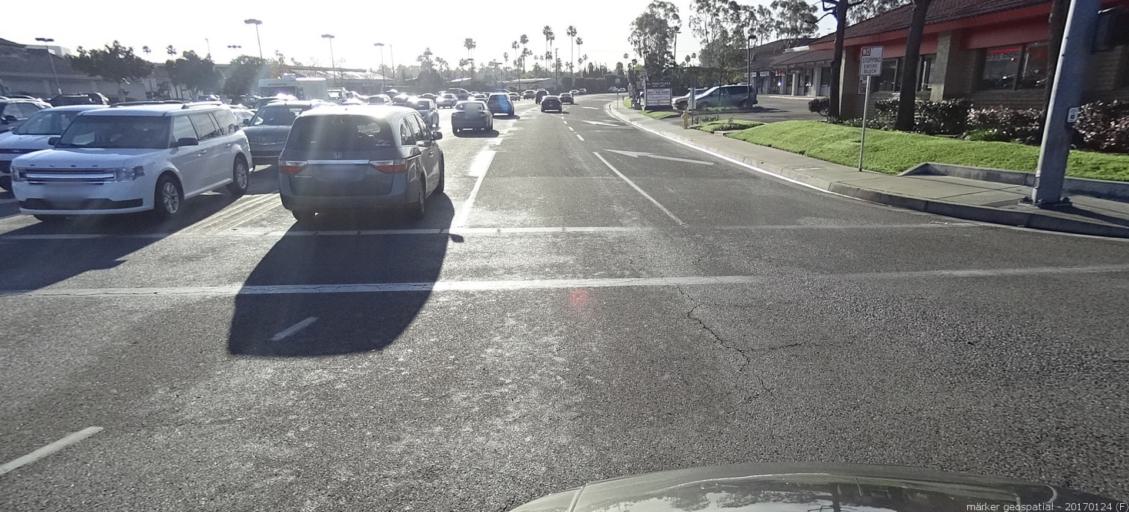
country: US
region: California
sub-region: Orange County
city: Laguna Hills
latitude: 33.6231
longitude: -117.6972
